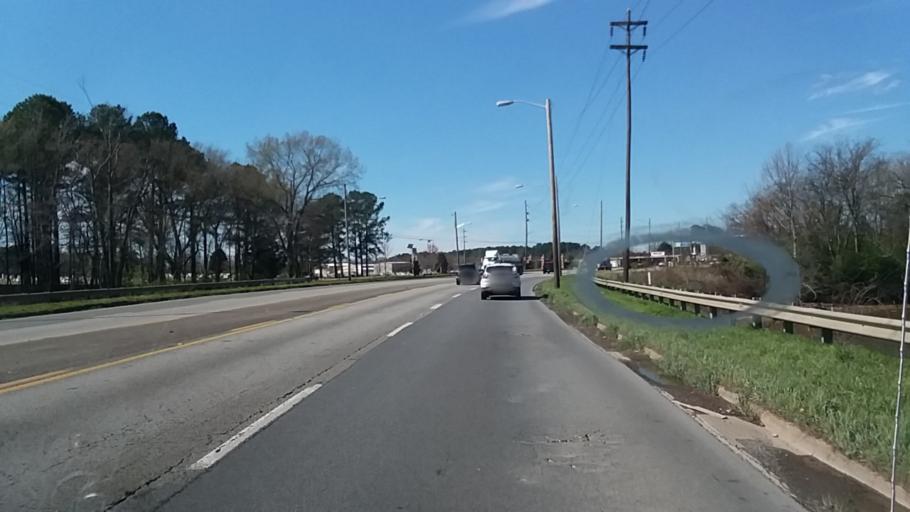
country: US
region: Alabama
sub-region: Morgan County
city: Decatur
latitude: 34.6196
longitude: -86.9994
